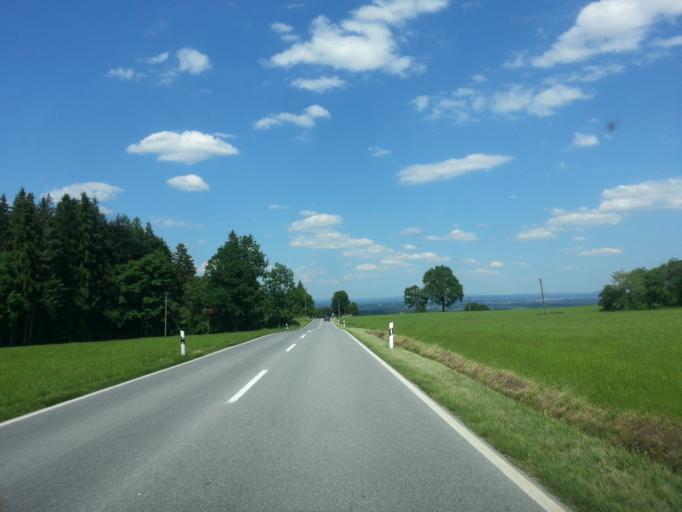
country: DE
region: Bavaria
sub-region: Upper Bavaria
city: Irschenberg
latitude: 47.8075
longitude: 11.9318
